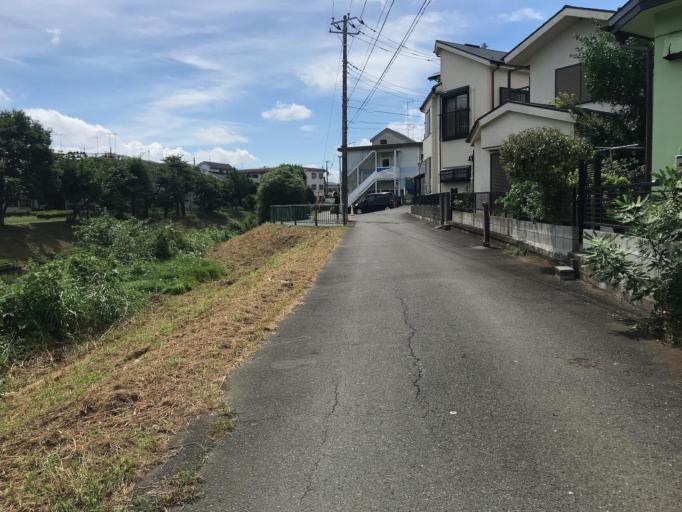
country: JP
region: Tokyo
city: Tanashicho
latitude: 35.7648
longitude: 139.5481
